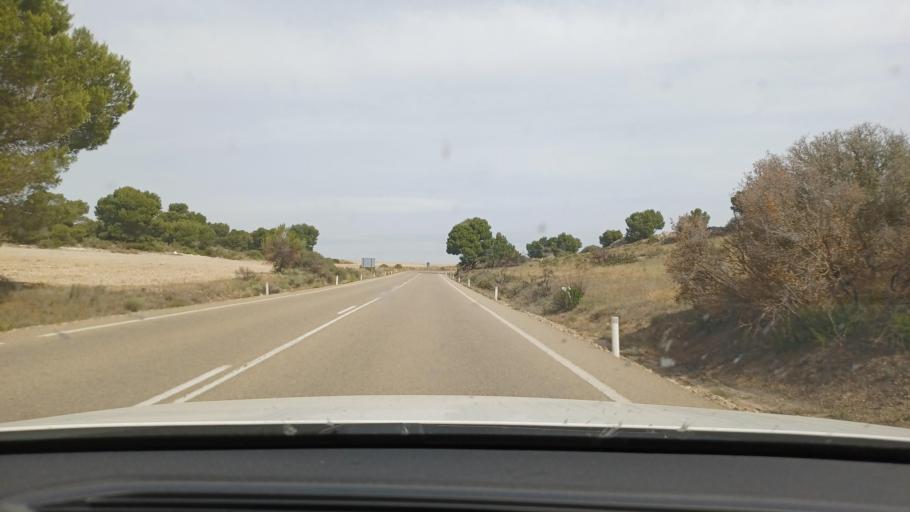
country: ES
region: Aragon
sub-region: Provincia de Zaragoza
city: Chiprana
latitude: 41.3622
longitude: -0.1056
